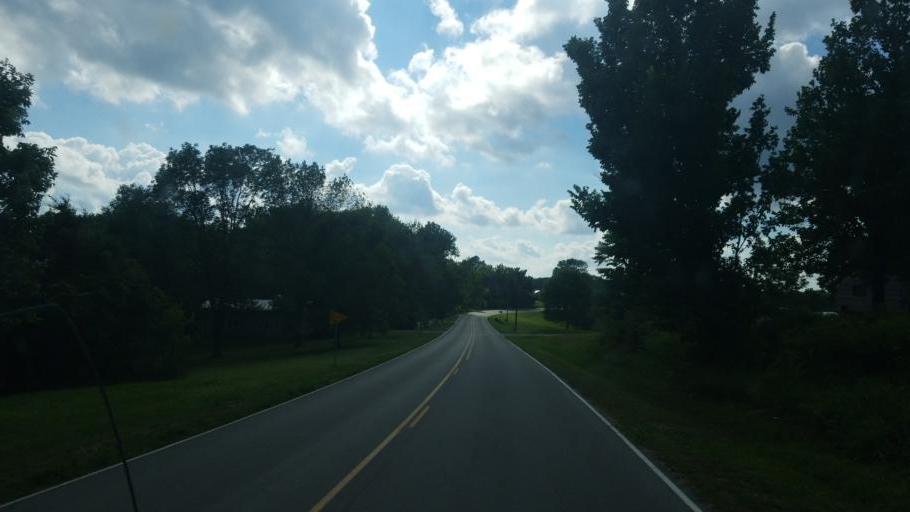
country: US
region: Illinois
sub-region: Union County
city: Cobden
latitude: 37.5461
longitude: -89.2805
